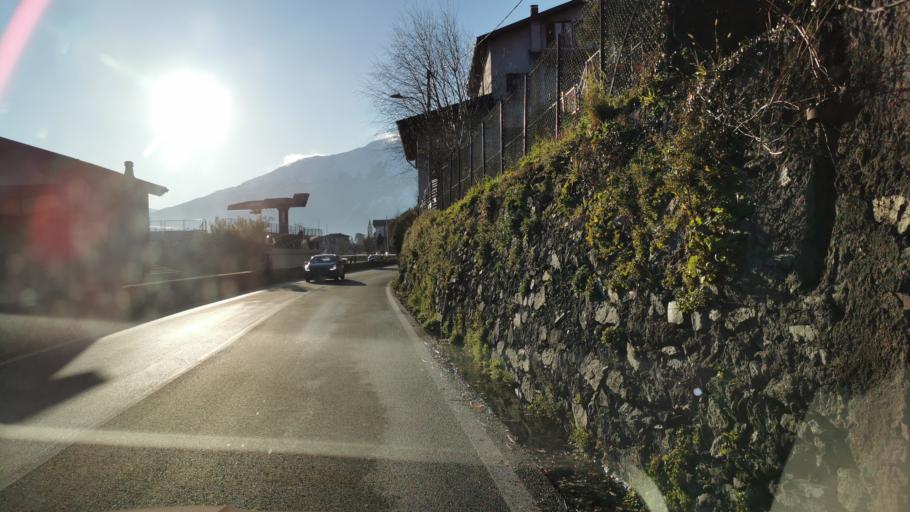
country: IT
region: Lombardy
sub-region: Provincia di Como
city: Vercana
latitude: 46.1591
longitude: 9.3415
